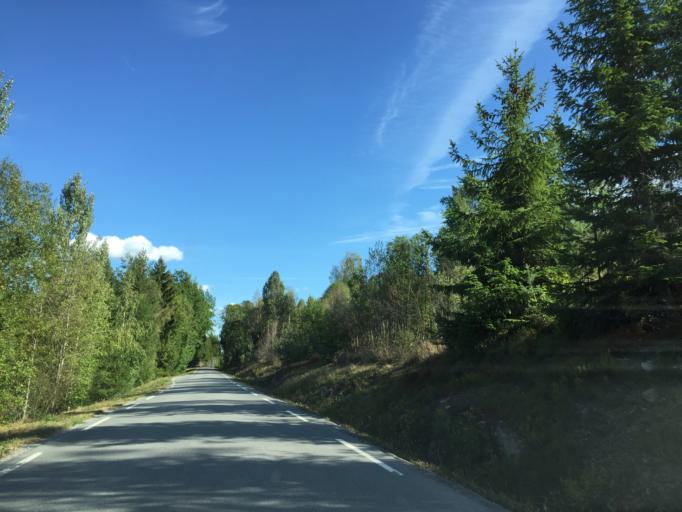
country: NO
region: Buskerud
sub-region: Ovre Eiker
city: Hokksund
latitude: 59.6609
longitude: 9.8991
